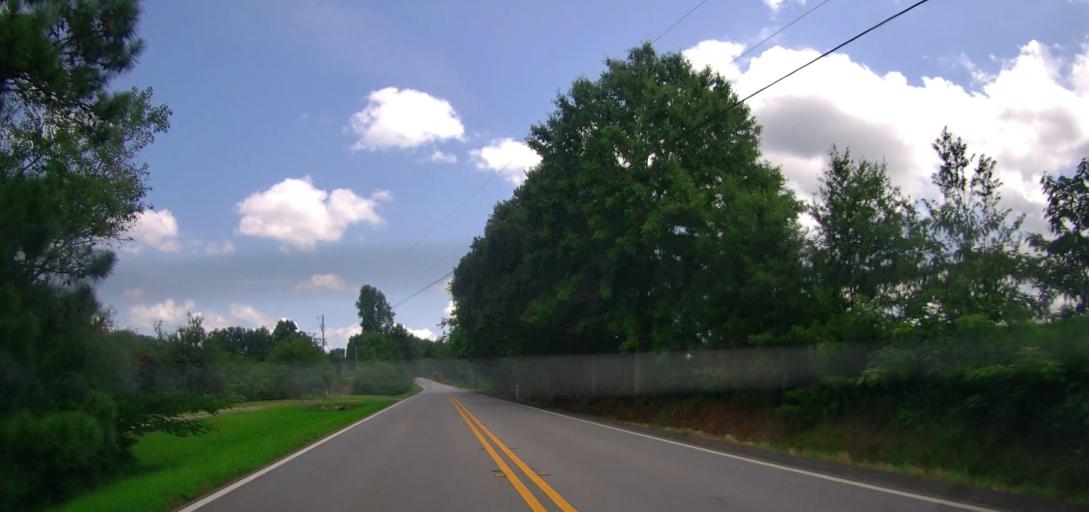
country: US
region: Georgia
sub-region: Carroll County
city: Bowdon
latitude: 33.4382
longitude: -85.2754
